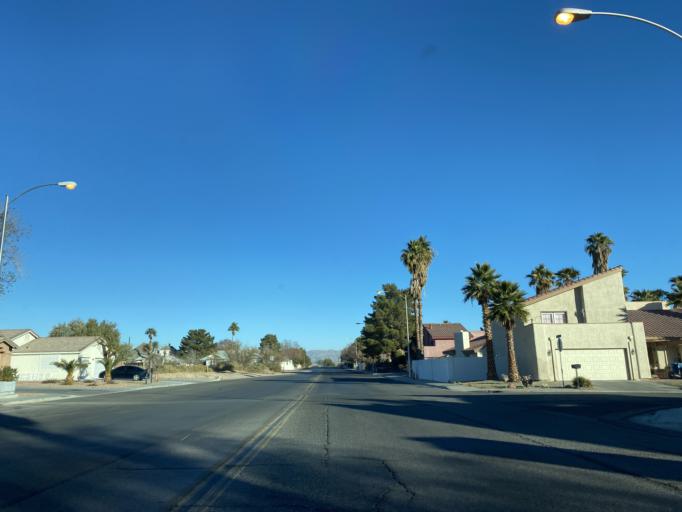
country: US
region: Nevada
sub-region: Clark County
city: Winchester
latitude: 36.1206
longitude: -115.1098
